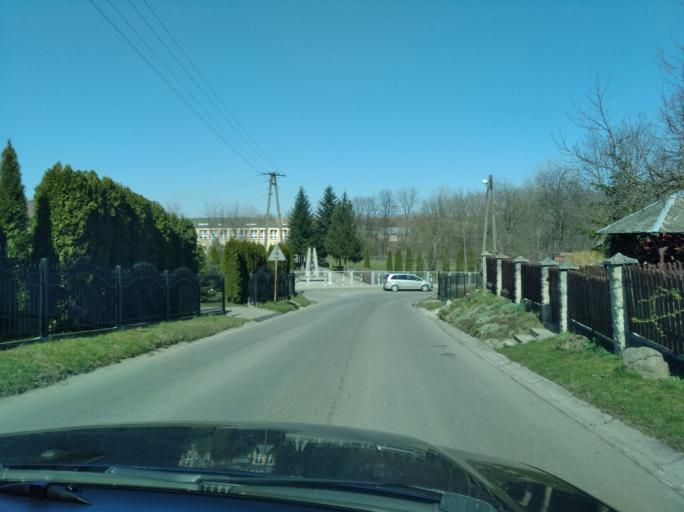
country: PL
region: Subcarpathian Voivodeship
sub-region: Powiat przeworski
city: Pantalowice
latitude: 49.9516
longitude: 22.4358
